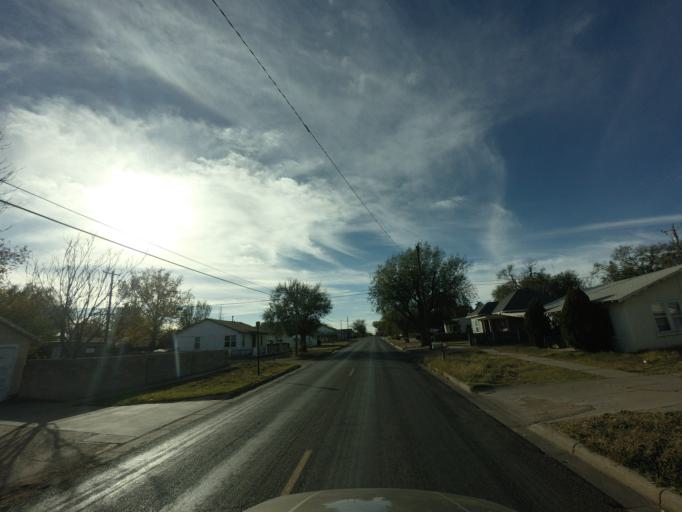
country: US
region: New Mexico
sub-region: Curry County
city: Clovis
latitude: 34.4120
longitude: -103.1994
